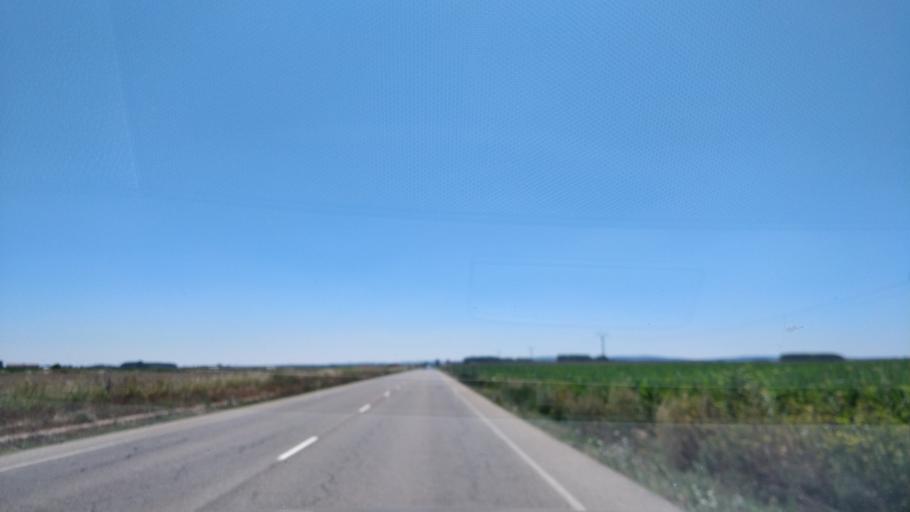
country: ES
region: Castille and Leon
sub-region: Provincia de Leon
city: Soto de la Vega
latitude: 42.3598
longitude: -5.8898
